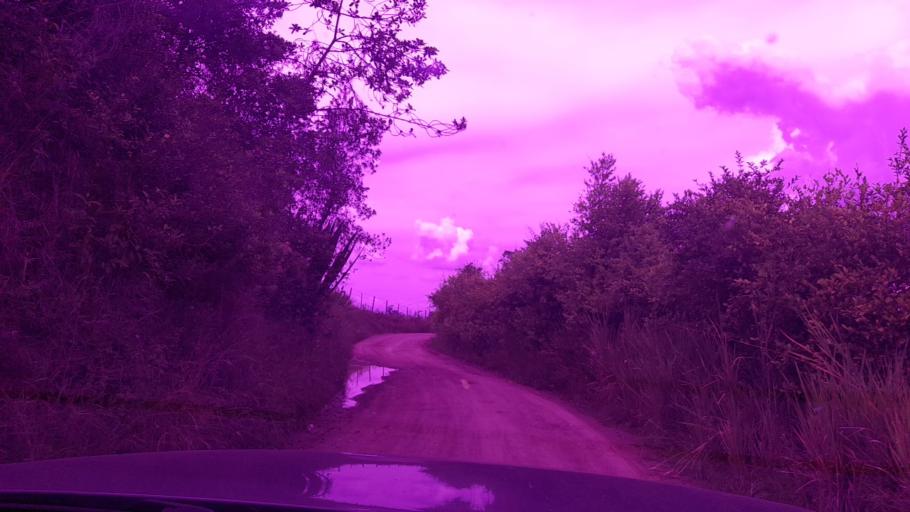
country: CO
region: Valle del Cauca
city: Andalucia
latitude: 4.1719
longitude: -76.1195
